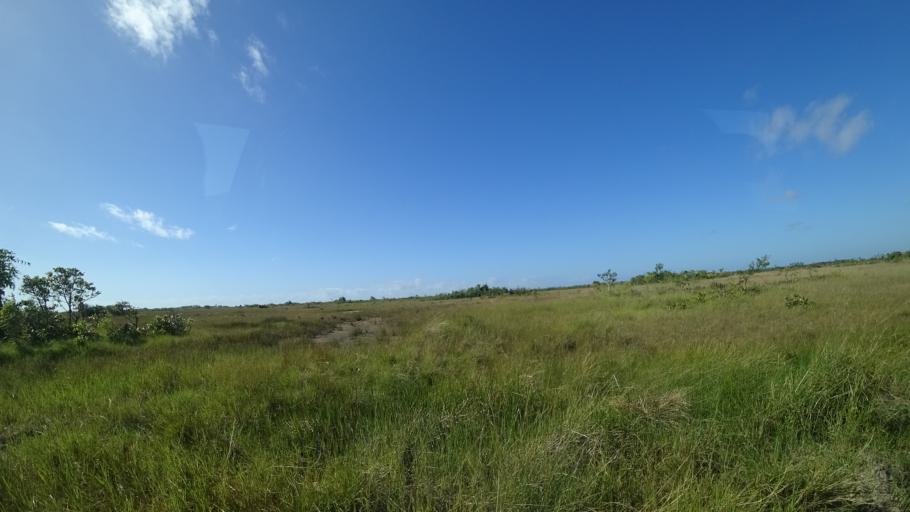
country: MZ
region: Sofala
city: Beira
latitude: -19.6991
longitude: 35.0289
